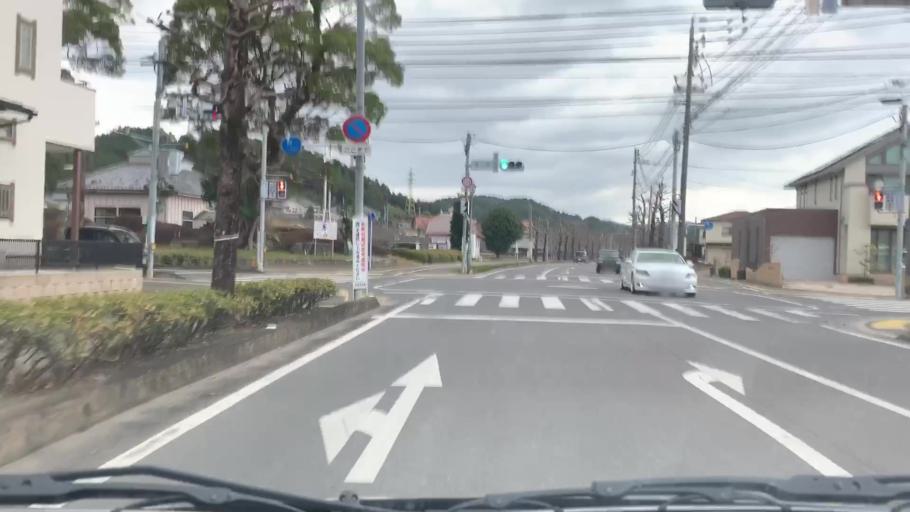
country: JP
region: Saga Prefecture
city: Ureshinomachi-shimojuku
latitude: 33.1020
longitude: 129.9866
